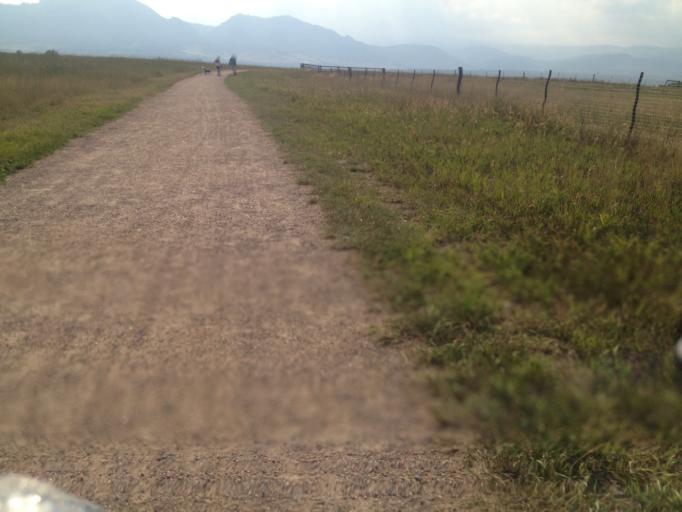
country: US
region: Colorado
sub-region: Boulder County
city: Superior
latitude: 39.9781
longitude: -105.1695
